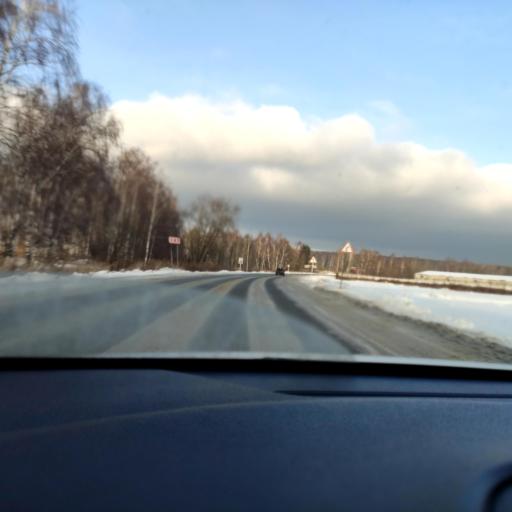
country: RU
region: Tatarstan
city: Osinovo
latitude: 55.8936
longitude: 48.8898
